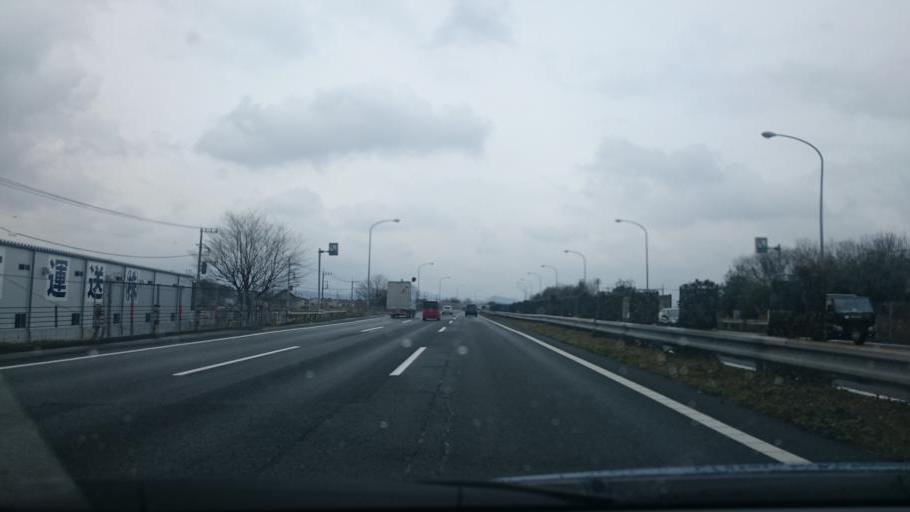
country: JP
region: Saitama
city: Ogawa
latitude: 36.0442
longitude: 139.3580
